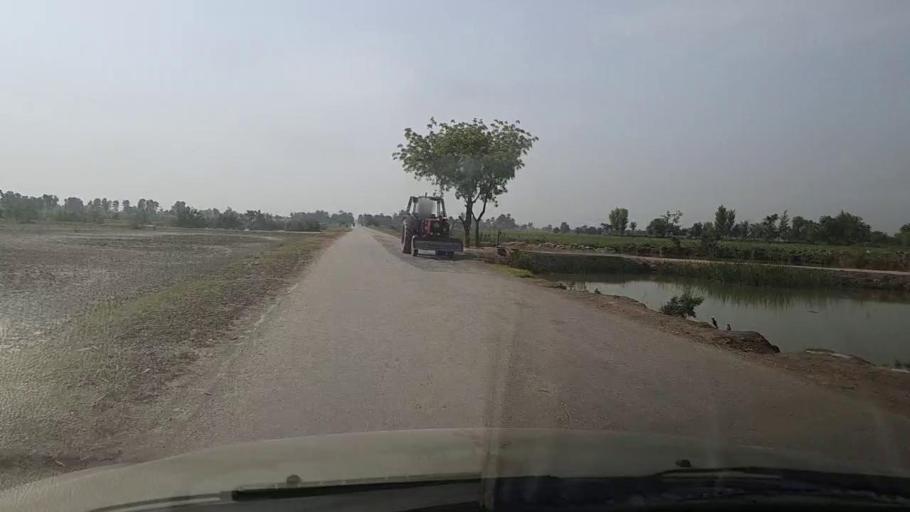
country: PK
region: Sindh
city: Gambat
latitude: 27.4737
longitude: 68.4732
